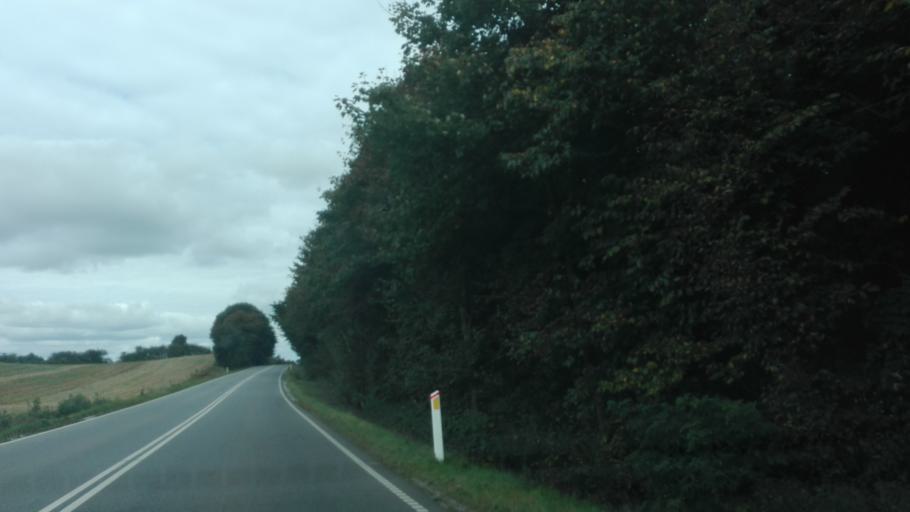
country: DK
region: Central Jutland
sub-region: Skanderborg Kommune
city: Stilling
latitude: 56.0992
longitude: 9.9705
